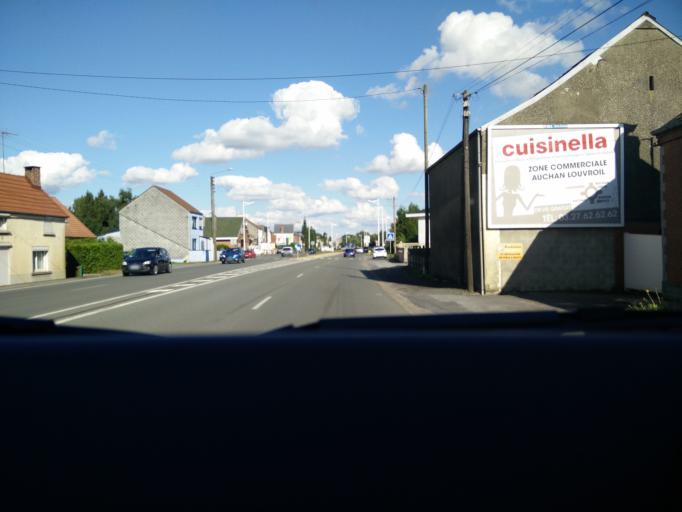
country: FR
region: Nord-Pas-de-Calais
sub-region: Departement du Nord
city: Feignies
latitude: 50.2803
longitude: 3.9203
